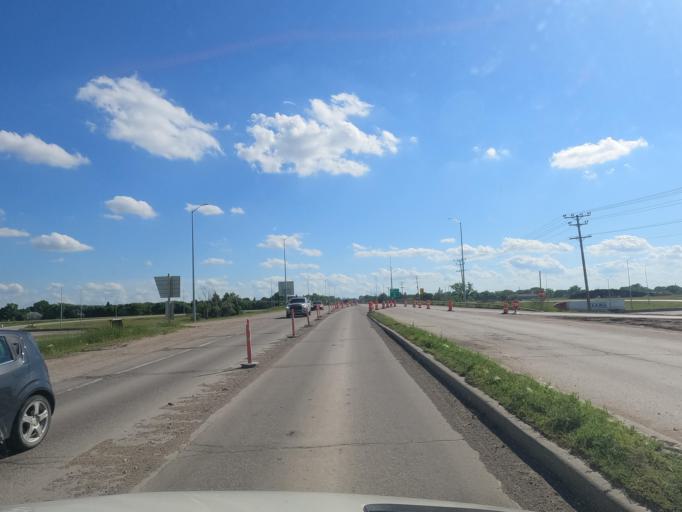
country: CA
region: Manitoba
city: Winnipeg
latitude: 49.9728
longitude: -97.0732
